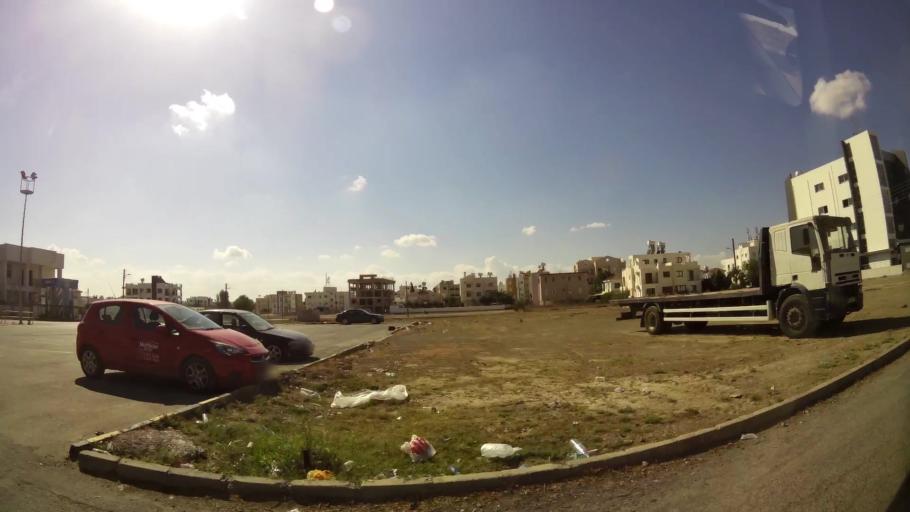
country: CY
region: Lefkosia
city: Nicosia
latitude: 35.2123
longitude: 33.3315
